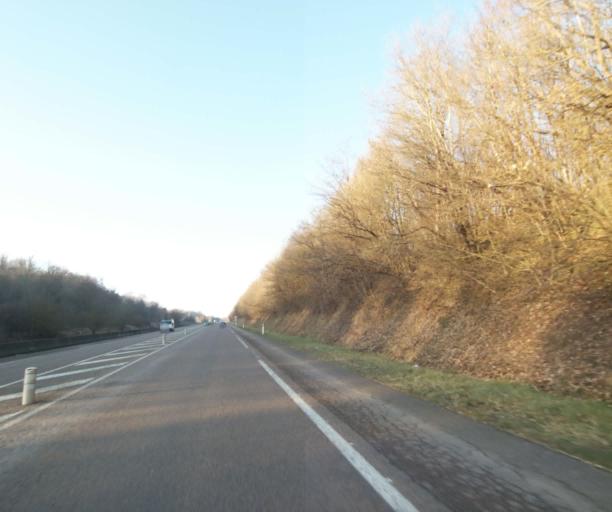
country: FR
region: Champagne-Ardenne
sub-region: Departement de la Haute-Marne
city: Chevillon
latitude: 48.5026
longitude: 5.1040
